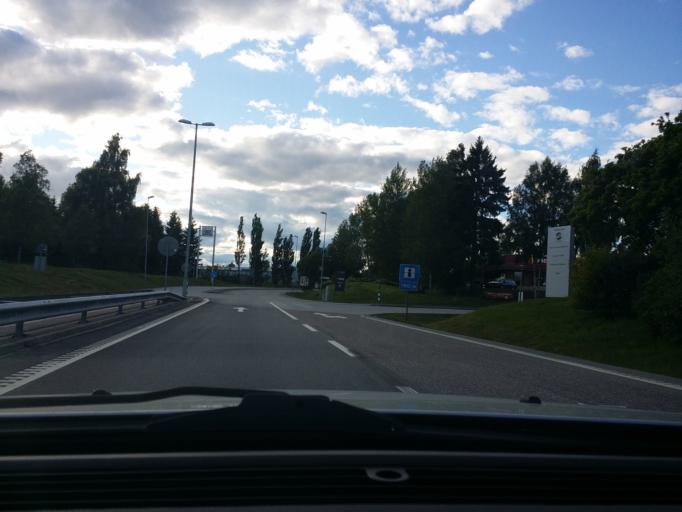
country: SE
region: Stockholm
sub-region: Sigtuna Kommun
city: Rosersberg
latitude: 59.6069
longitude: 17.8947
